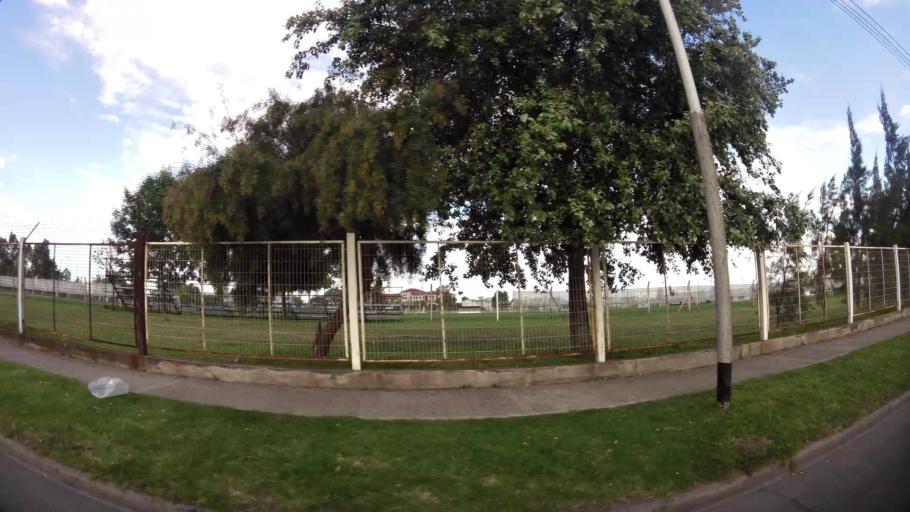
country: AR
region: Buenos Aires
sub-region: Partido de Avellaneda
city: Avellaneda
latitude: -34.6819
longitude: -58.3638
